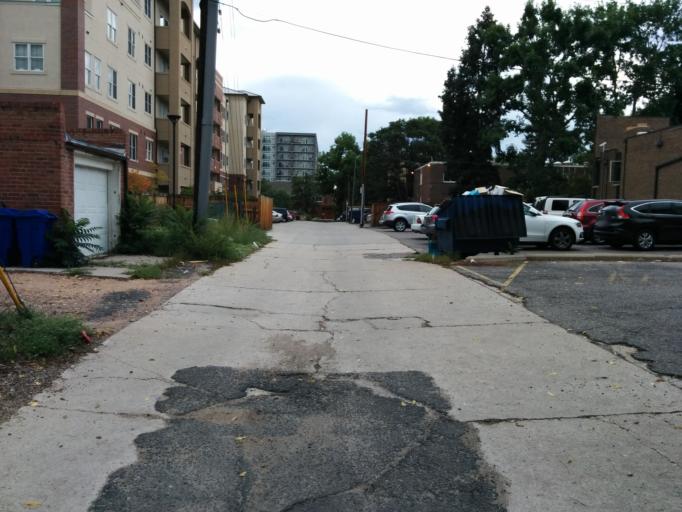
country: US
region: Colorado
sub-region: Arapahoe County
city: Cherry Hills Village
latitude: 39.6753
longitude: -104.9587
